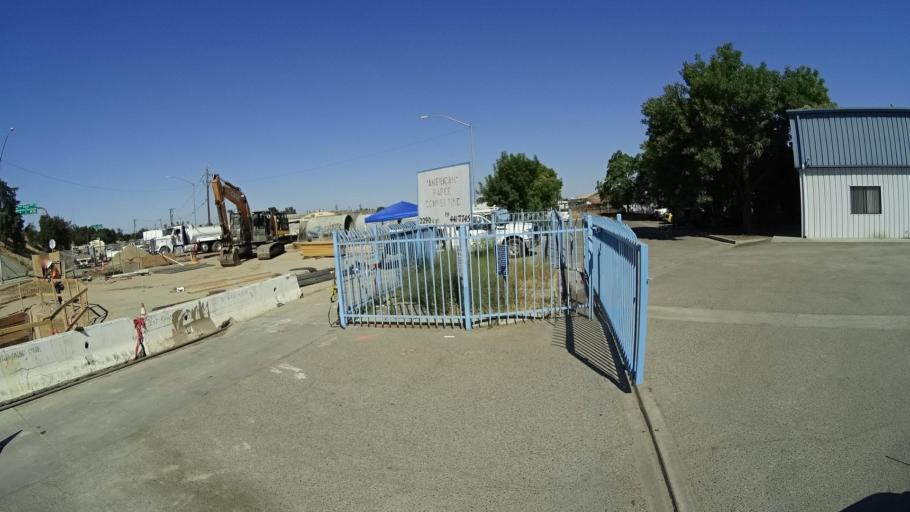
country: US
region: California
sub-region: Fresno County
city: Fresno
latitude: 36.7444
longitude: -119.8094
